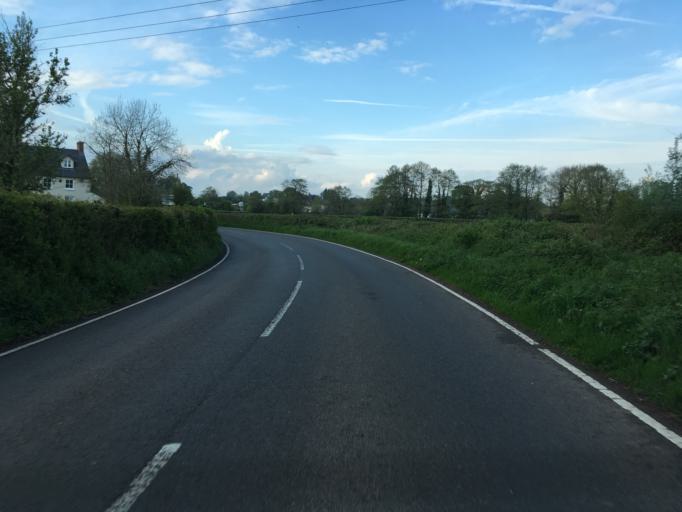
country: GB
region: Wales
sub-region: Monmouthshire
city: Llanarth
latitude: 51.7608
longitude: -2.8499
